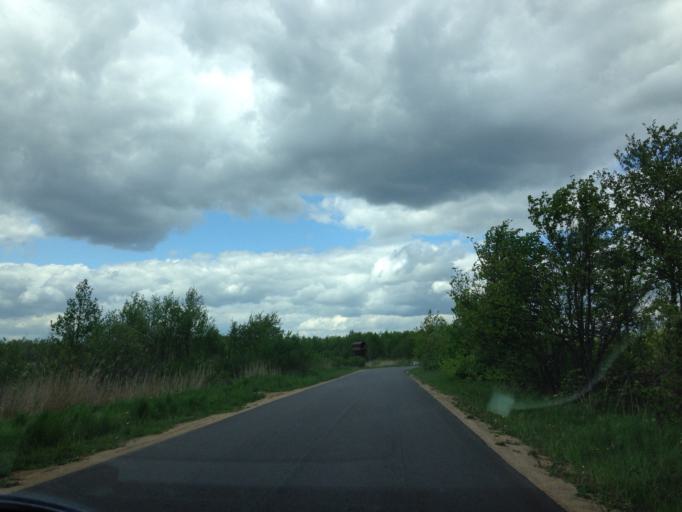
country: PL
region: Podlasie
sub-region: Powiat bialostocki
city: Tykocin
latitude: 53.2972
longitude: 22.6056
